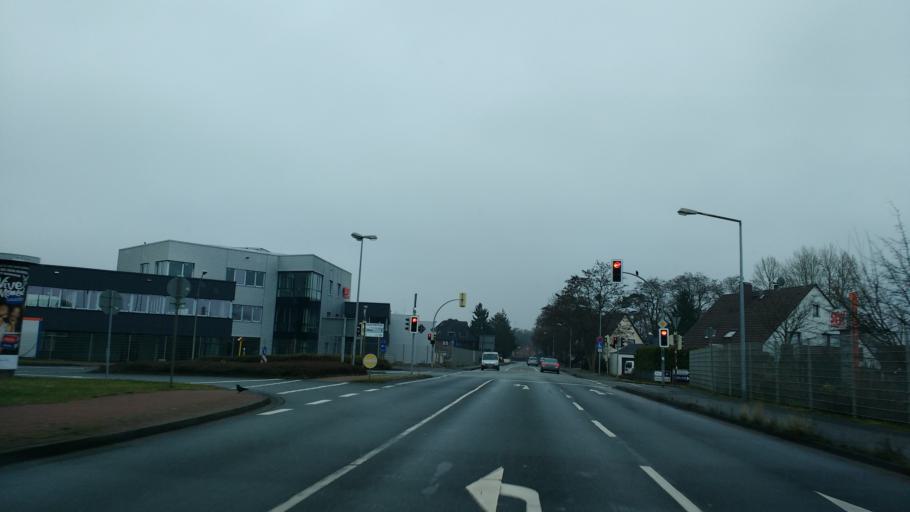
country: DE
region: Lower Saxony
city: Garbsen
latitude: 52.4191
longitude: 9.5744
